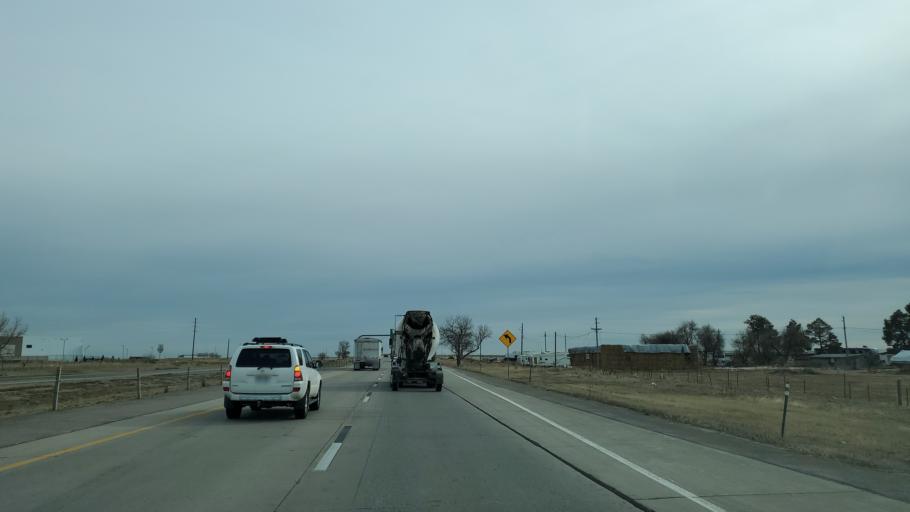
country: US
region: Colorado
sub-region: Adams County
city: Aurora
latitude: 39.7430
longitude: -104.7377
